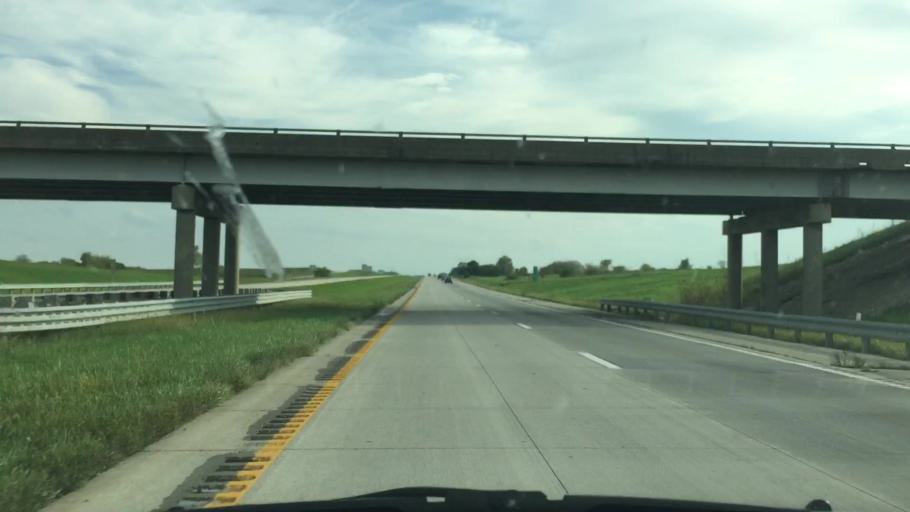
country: US
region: Missouri
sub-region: Harrison County
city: Bethany
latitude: 40.0768
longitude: -94.0935
